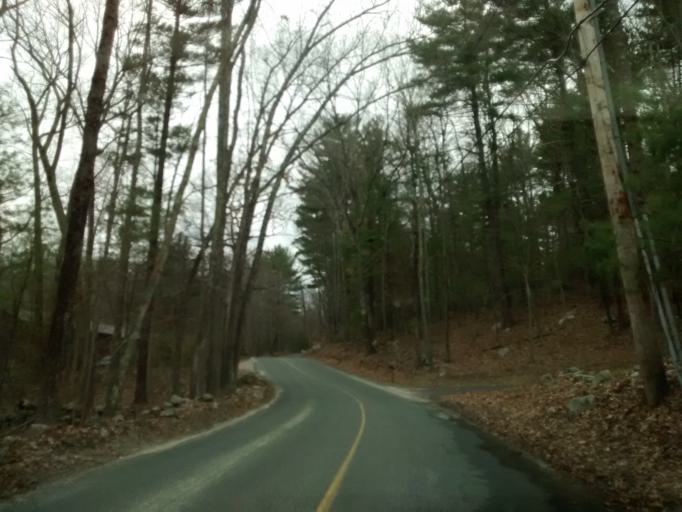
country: US
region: Massachusetts
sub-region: Worcester County
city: Charlton
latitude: 42.1245
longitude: -72.0121
